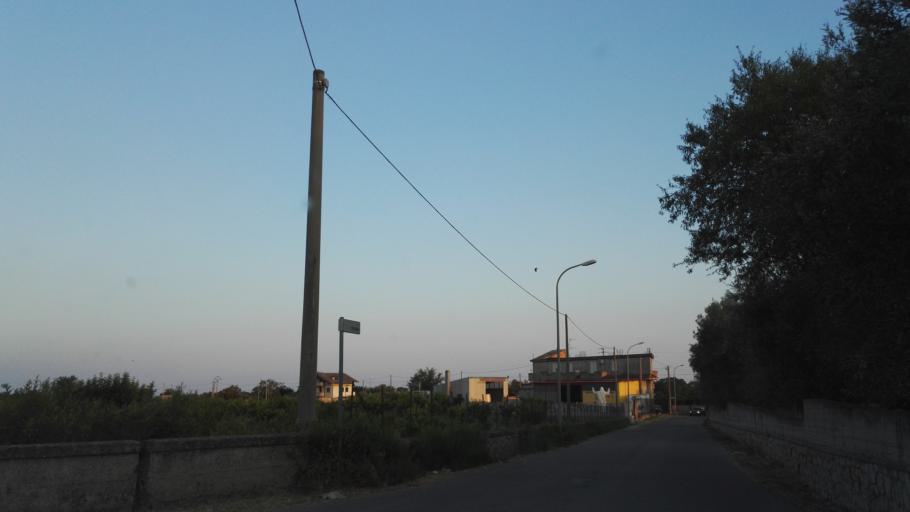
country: IT
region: Calabria
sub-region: Provincia di Reggio Calabria
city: Caulonia Marina
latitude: 38.3616
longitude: 16.4690
